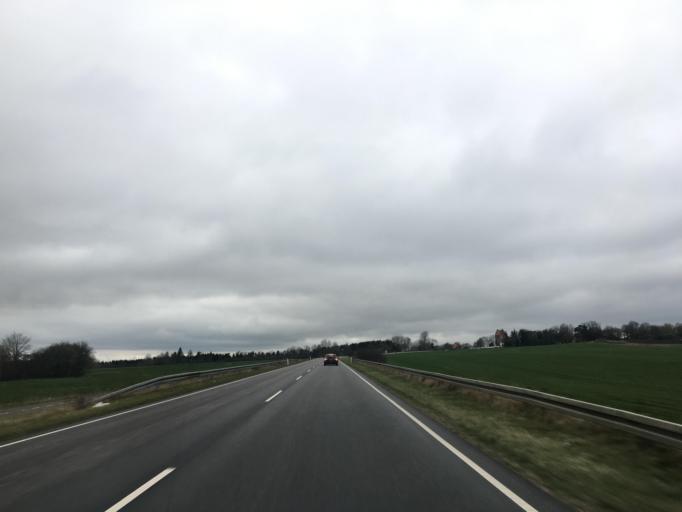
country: DK
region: Zealand
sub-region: Holbaek Kommune
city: Holbaek
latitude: 55.7397
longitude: 11.6238
